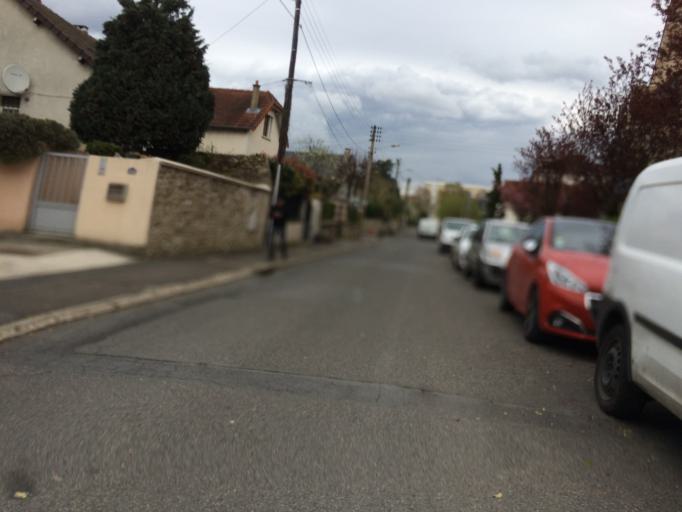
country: FR
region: Ile-de-France
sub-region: Departement de l'Essonne
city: Massy
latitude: 48.7314
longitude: 2.2800
